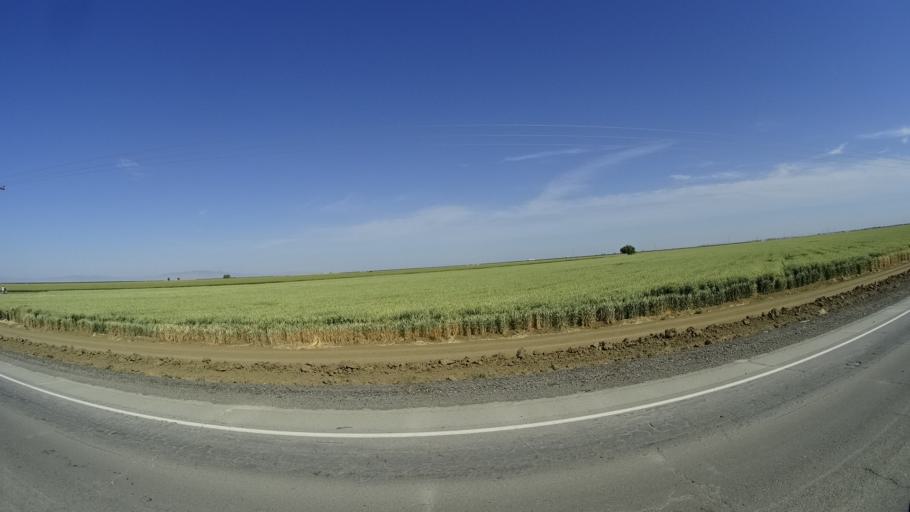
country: US
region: California
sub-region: Kings County
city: Lemoore Station
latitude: 36.2076
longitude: -119.9220
